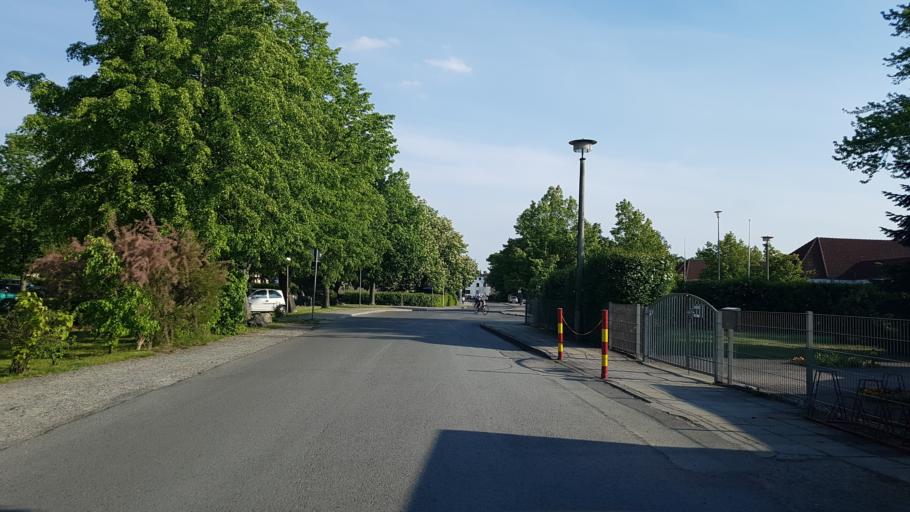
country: DE
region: Brandenburg
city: Elsterwerda
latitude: 51.4634
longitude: 13.5107
